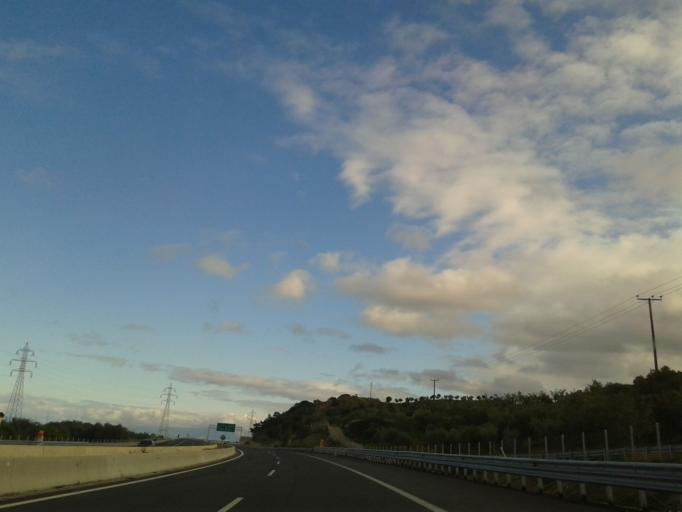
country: GR
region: Peloponnese
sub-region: Nomos Korinthias
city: Xylokastro
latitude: 38.0788
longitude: 22.5994
